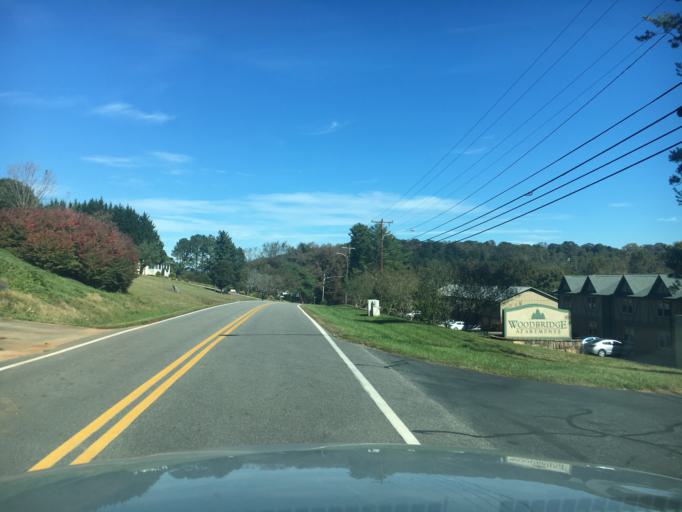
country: US
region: North Carolina
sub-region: Burke County
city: Morganton
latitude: 35.7309
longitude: -81.7136
